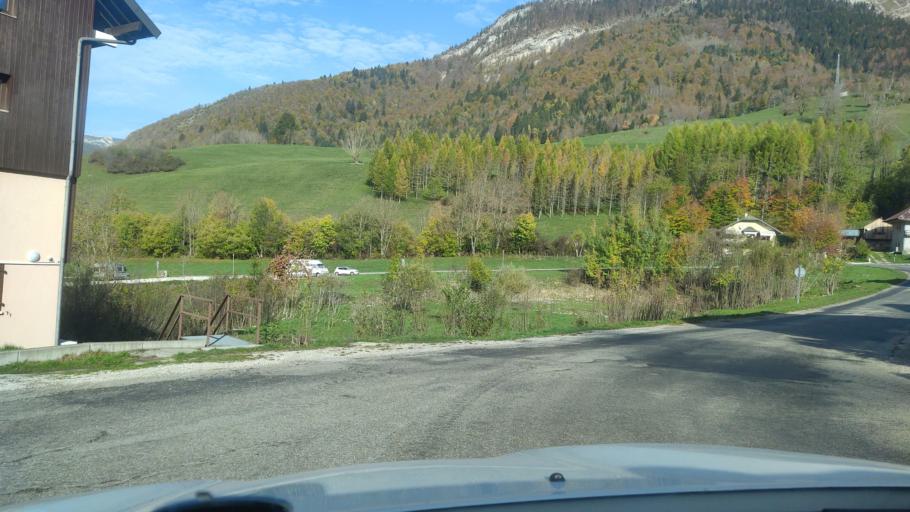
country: FR
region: Rhone-Alpes
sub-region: Departement de la Savoie
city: Cruet
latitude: 45.6087
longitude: 6.1053
